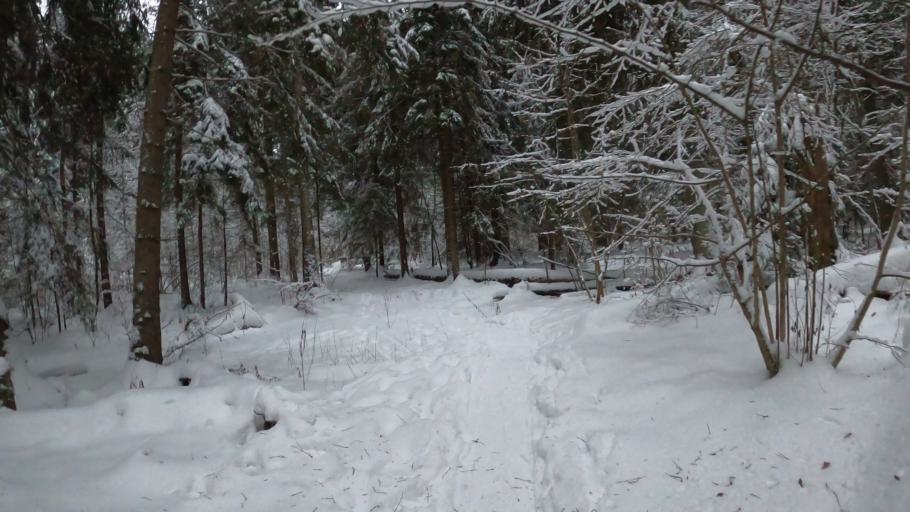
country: RU
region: Moskovskaya
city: Firsanovka
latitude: 55.9160
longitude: 37.2067
